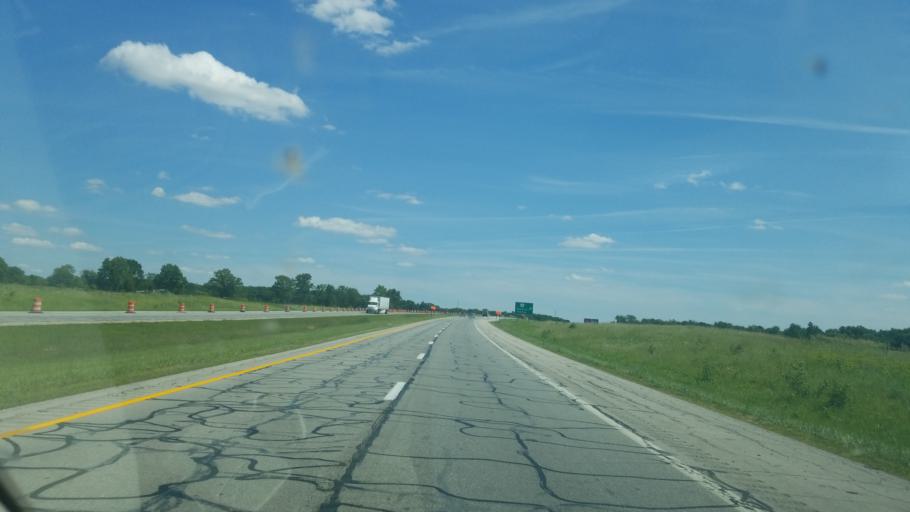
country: US
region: Ohio
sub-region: Marion County
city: Marion
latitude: 40.6701
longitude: -83.1148
